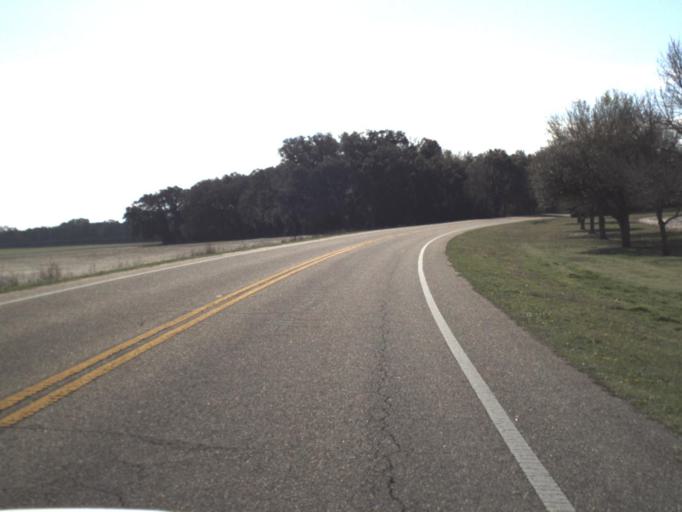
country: US
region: Florida
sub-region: Jackson County
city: Malone
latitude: 30.9718
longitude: -85.1645
